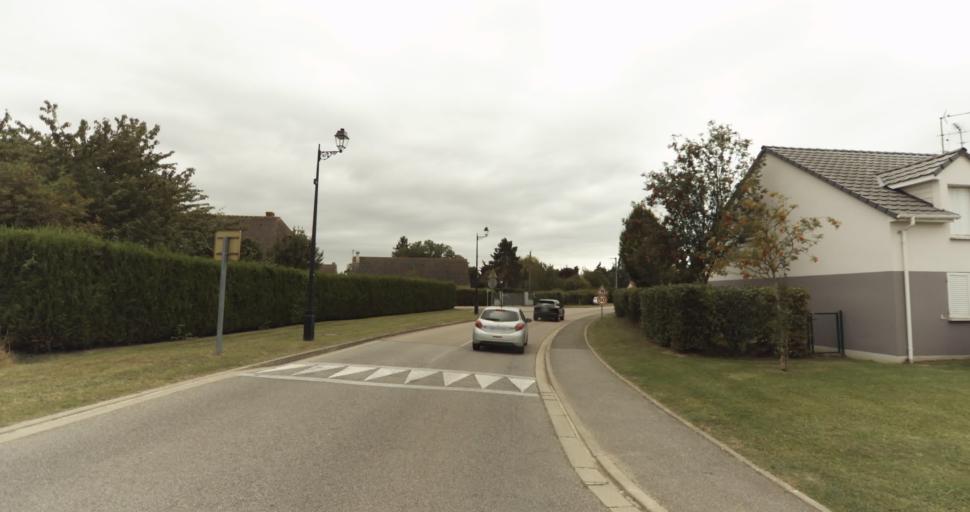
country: FR
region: Haute-Normandie
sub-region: Departement de l'Eure
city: Gravigny
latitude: 49.0392
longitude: 1.2104
